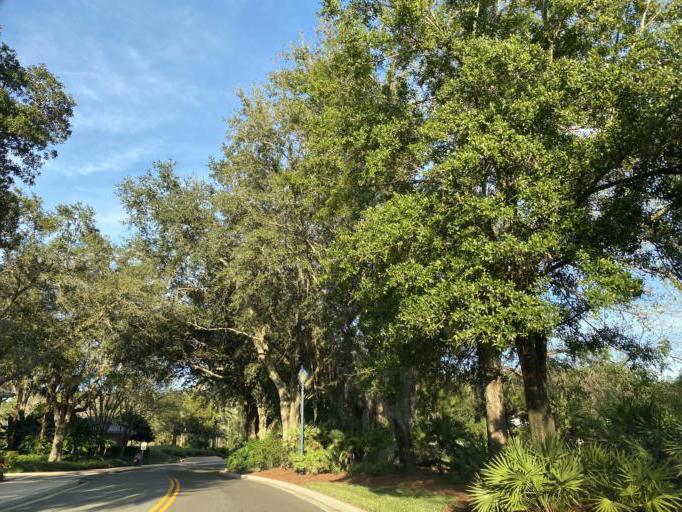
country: US
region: Florida
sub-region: Osceola County
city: Celebration
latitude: 28.3722
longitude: -81.5320
